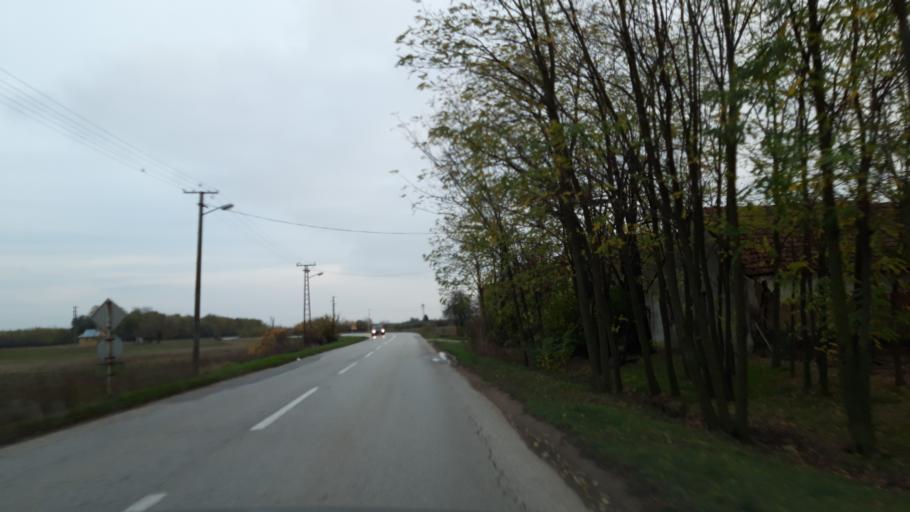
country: RS
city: Sanad
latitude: 45.9771
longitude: 20.1163
